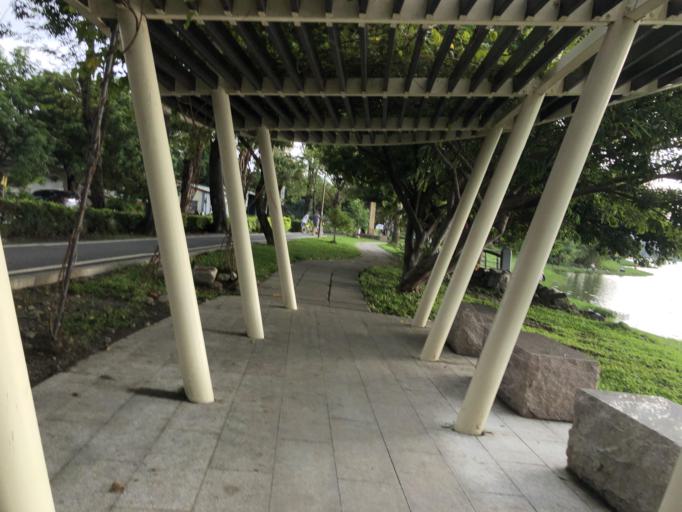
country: TW
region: Kaohsiung
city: Kaohsiung
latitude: 22.6860
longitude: 120.2998
